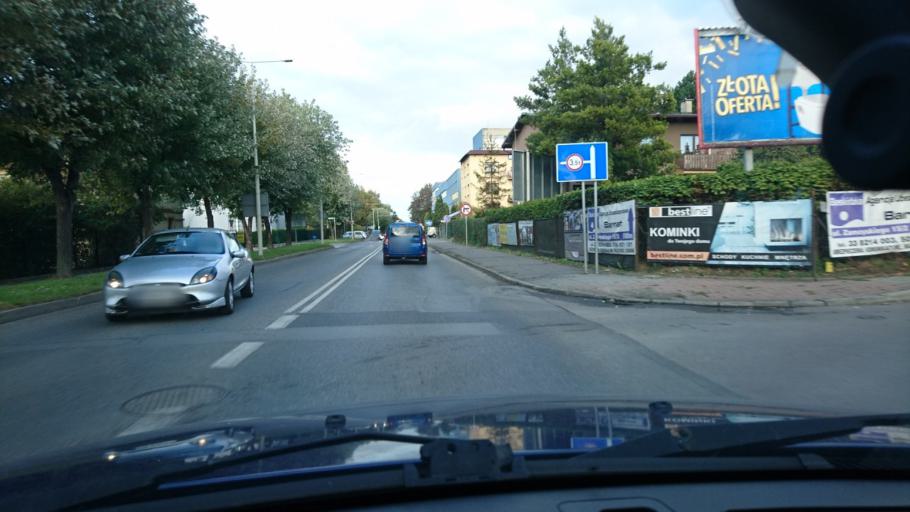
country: PL
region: Silesian Voivodeship
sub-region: Bielsko-Biala
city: Bielsko-Biala
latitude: 49.8239
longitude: 19.0272
